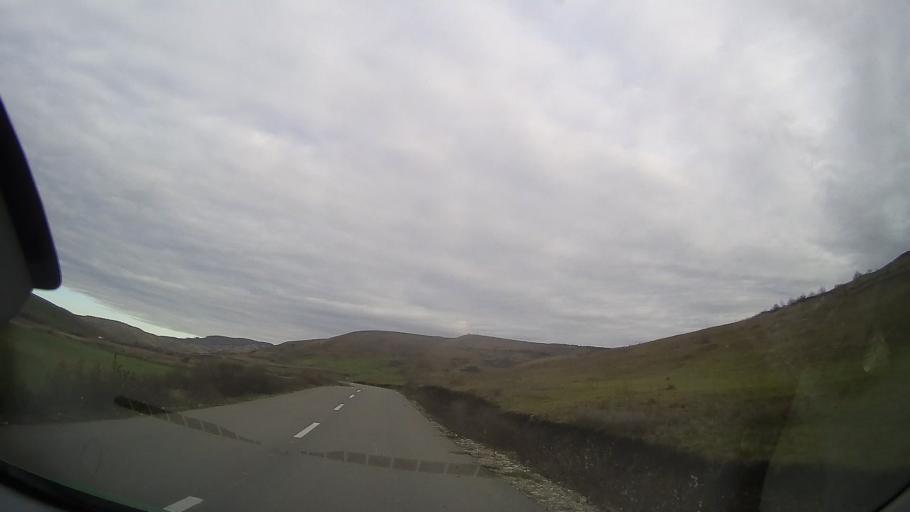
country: RO
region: Bistrita-Nasaud
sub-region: Comuna Silvasu de Campie
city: Silvasu de Campie
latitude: 46.7925
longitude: 24.2908
